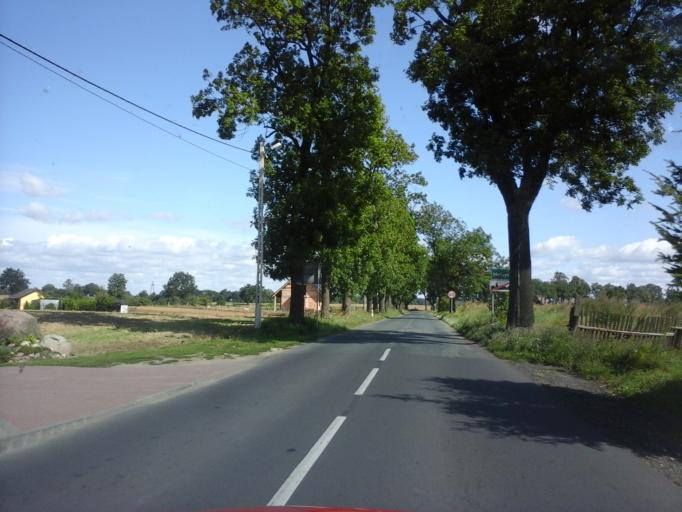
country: PL
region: West Pomeranian Voivodeship
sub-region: Powiat stargardzki
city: Dolice
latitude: 53.2126
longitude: 15.1490
